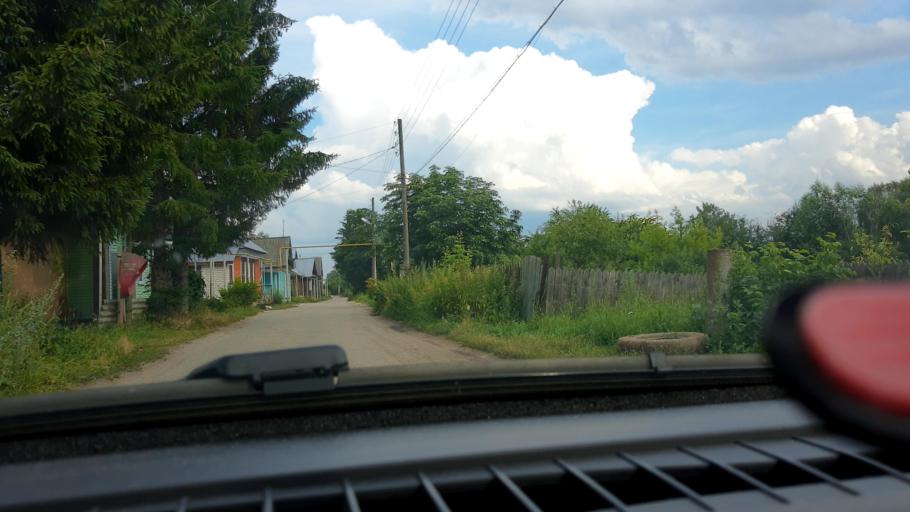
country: RU
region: Nizjnij Novgorod
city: Gorodets
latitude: 56.6171
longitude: 43.4959
